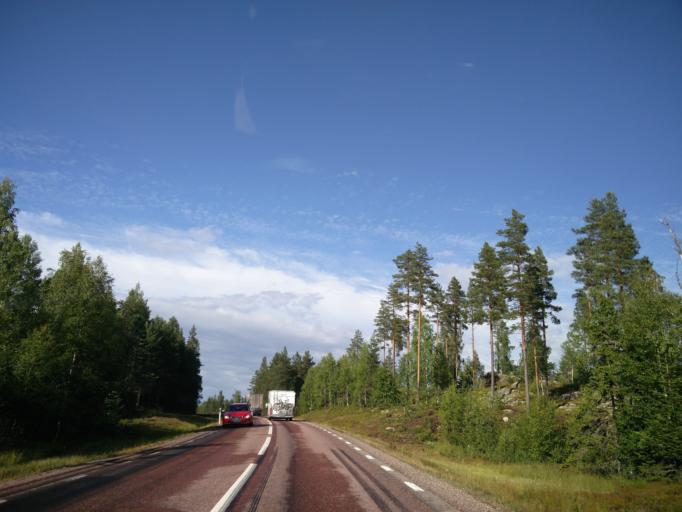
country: SE
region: Vaermland
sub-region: Hagfors Kommun
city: Ekshaerad
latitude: 60.4849
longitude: 13.4073
